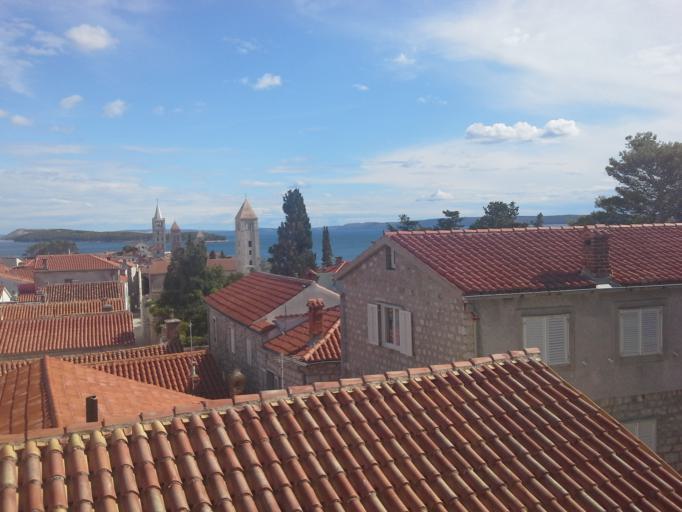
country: HR
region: Primorsko-Goranska
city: Banjol
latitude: 44.7574
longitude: 14.7588
